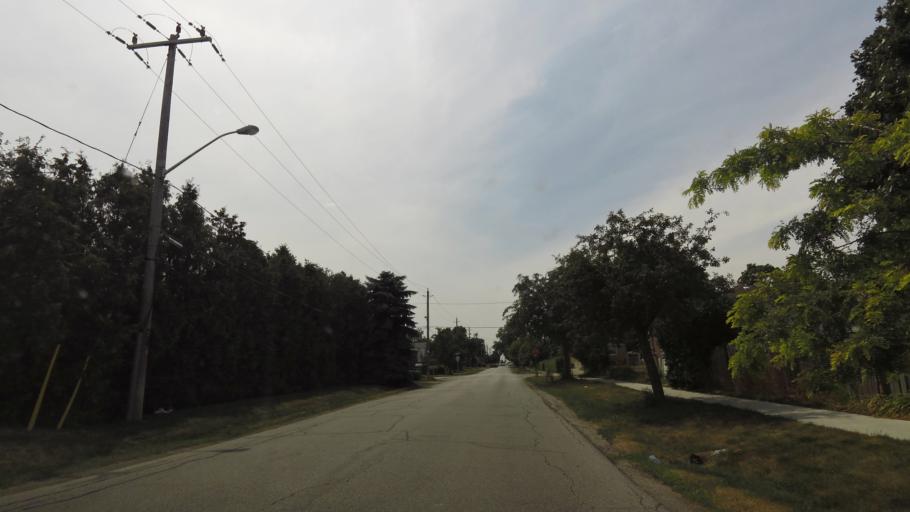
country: CA
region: Ontario
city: Etobicoke
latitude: 43.6238
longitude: -79.5232
